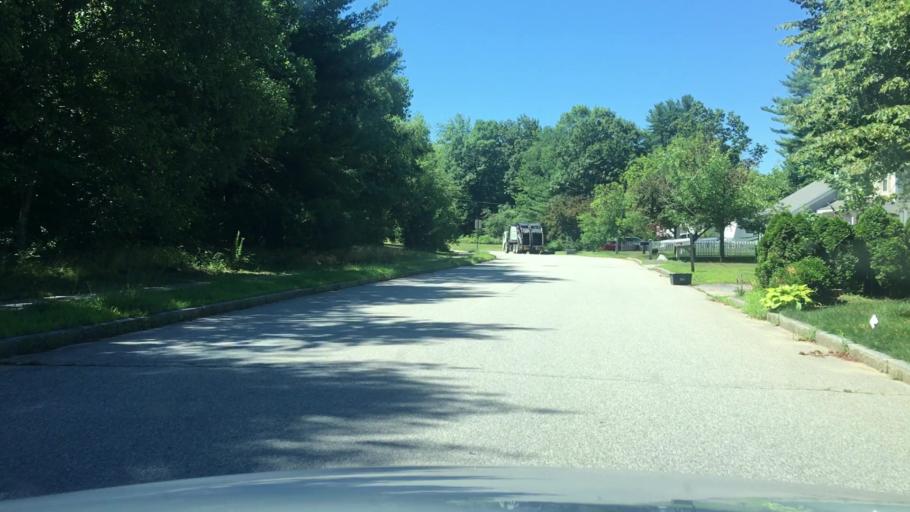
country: US
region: New Hampshire
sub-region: Merrimack County
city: Boscawen
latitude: 43.2706
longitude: -71.5997
